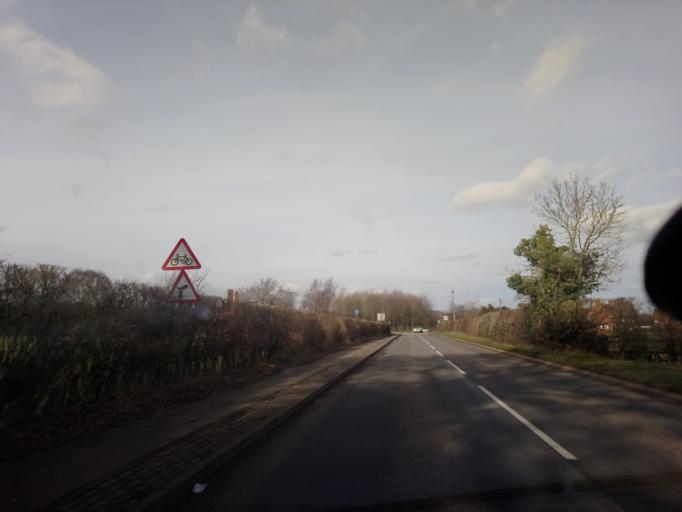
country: GB
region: England
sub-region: Shropshire
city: Stoke upon Tern
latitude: 52.8458
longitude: -2.5739
